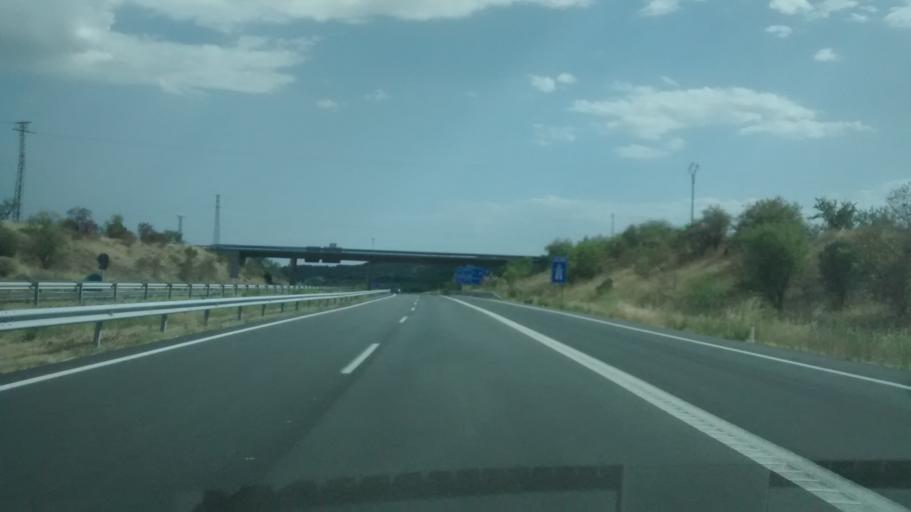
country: ES
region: La Rioja
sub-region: Provincia de La Rioja
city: Calahorra
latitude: 42.3044
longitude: -1.9818
